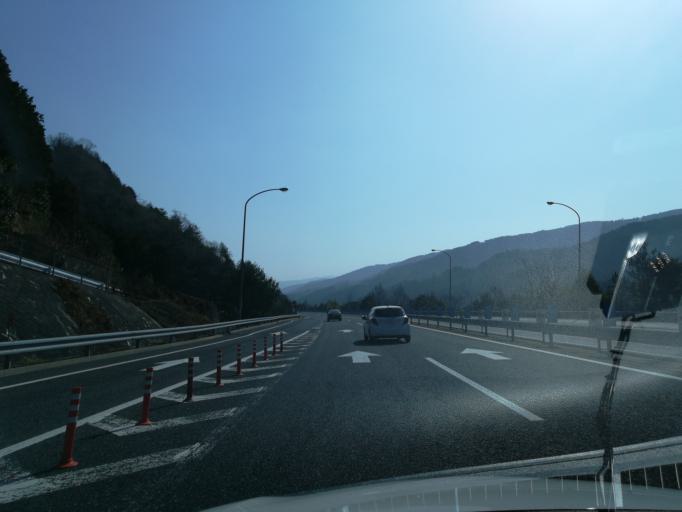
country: JP
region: Tokushima
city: Ikedacho
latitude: 34.0058
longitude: 133.7079
